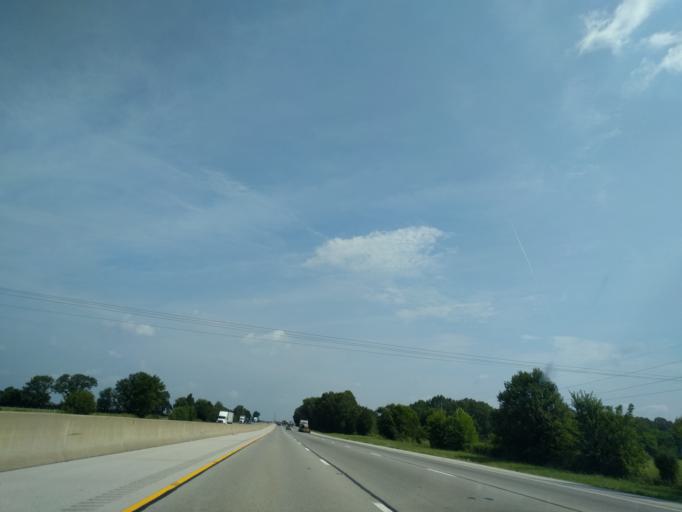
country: US
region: Kentucky
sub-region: Warren County
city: Plano
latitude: 36.8913
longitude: -86.4407
